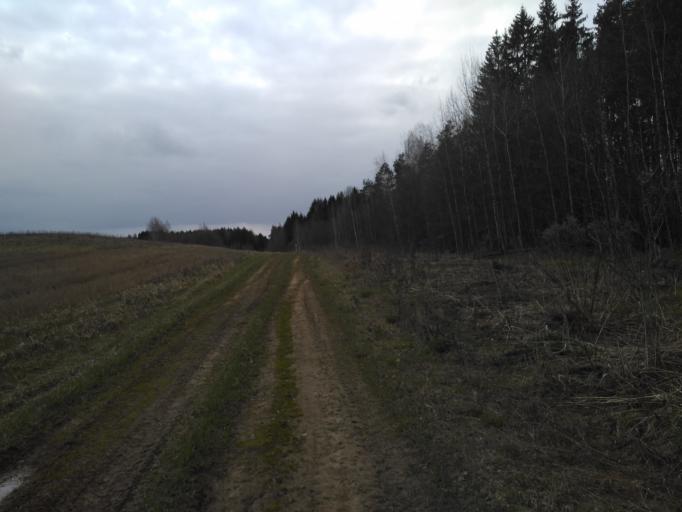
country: BY
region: Minsk
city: Korolev Stan
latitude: 54.0101
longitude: 27.8214
